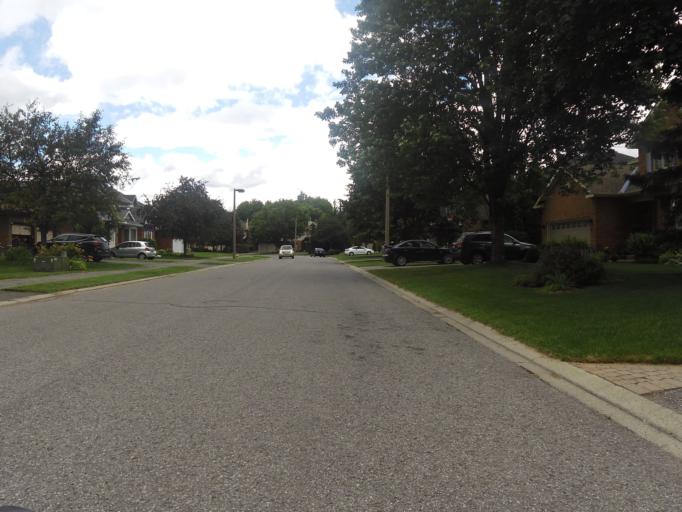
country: CA
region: Ontario
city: Bells Corners
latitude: 45.3192
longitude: -75.9124
